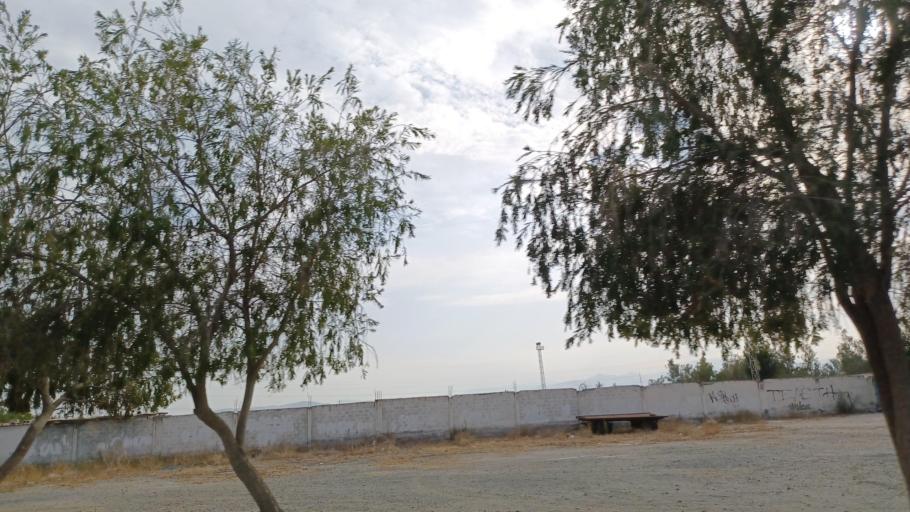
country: CY
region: Lefkosia
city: Peristerona
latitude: 35.1281
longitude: 33.0850
